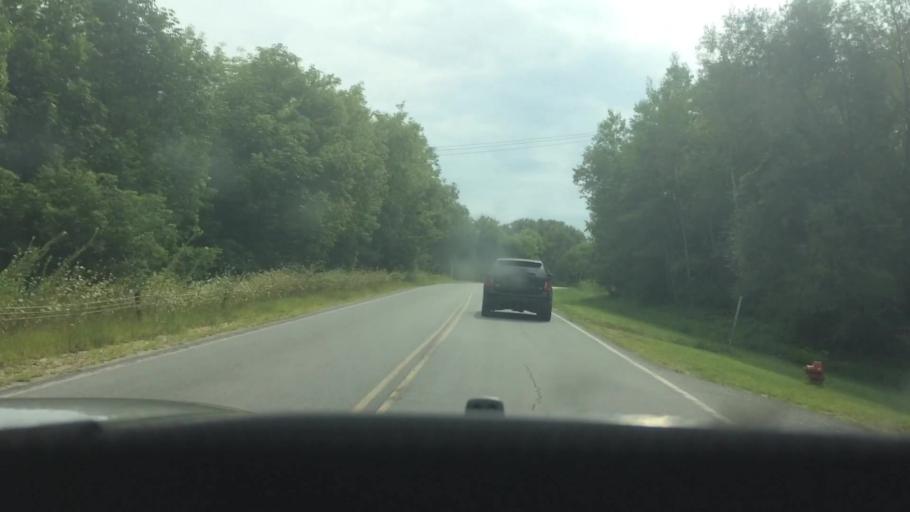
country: US
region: New York
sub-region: St. Lawrence County
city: Canton
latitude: 44.4702
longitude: -75.2348
